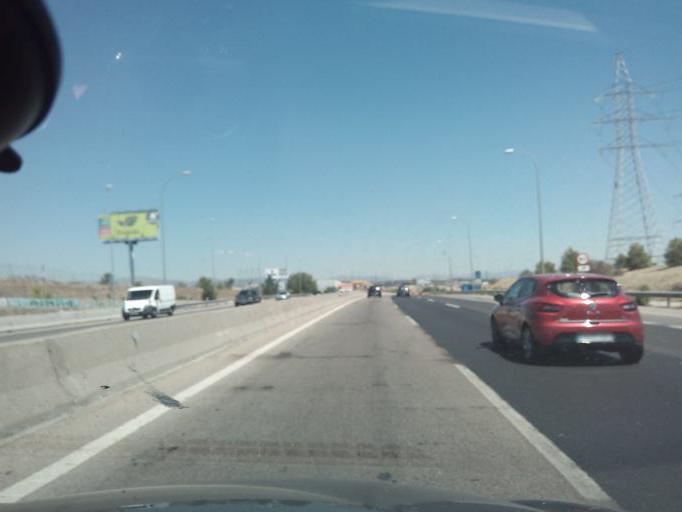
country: ES
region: Madrid
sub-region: Provincia de Madrid
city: San Sebastian de los Reyes
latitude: 40.5483
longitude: -3.6081
